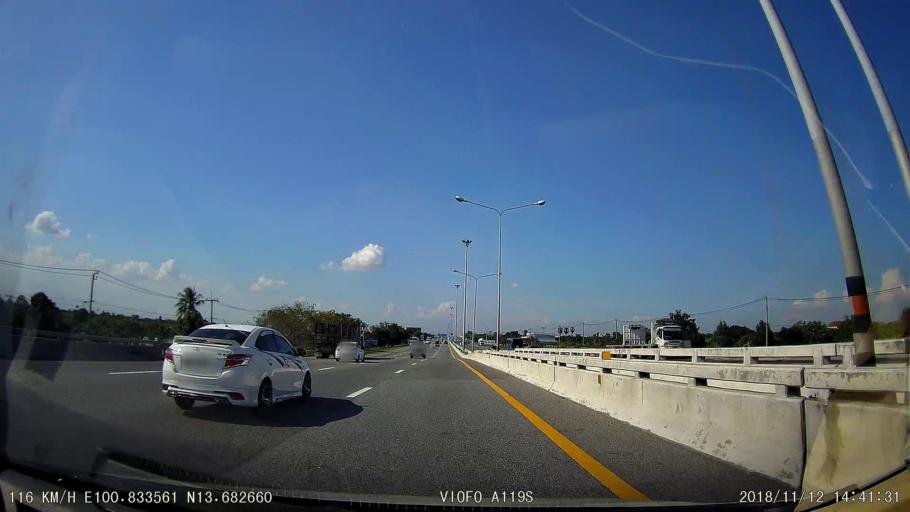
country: TH
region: Samut Prakan
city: Ban Khlong Bang Sao Thong
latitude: 13.6827
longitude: 100.8336
